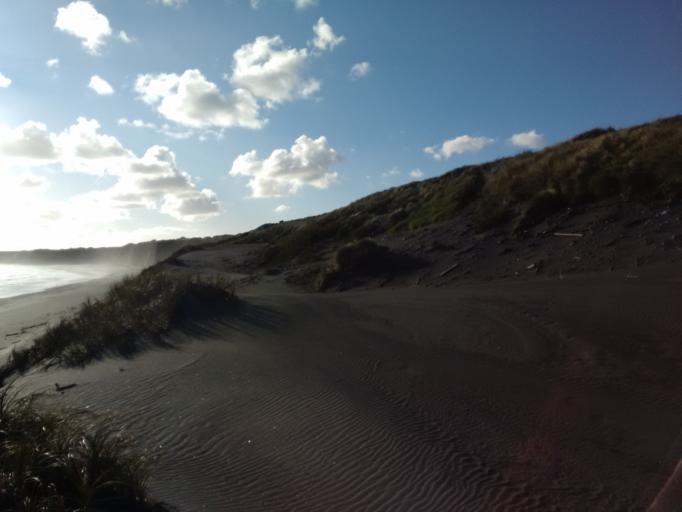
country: NZ
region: Taranaki
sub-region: South Taranaki District
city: Patea
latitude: -39.7718
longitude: 174.4858
